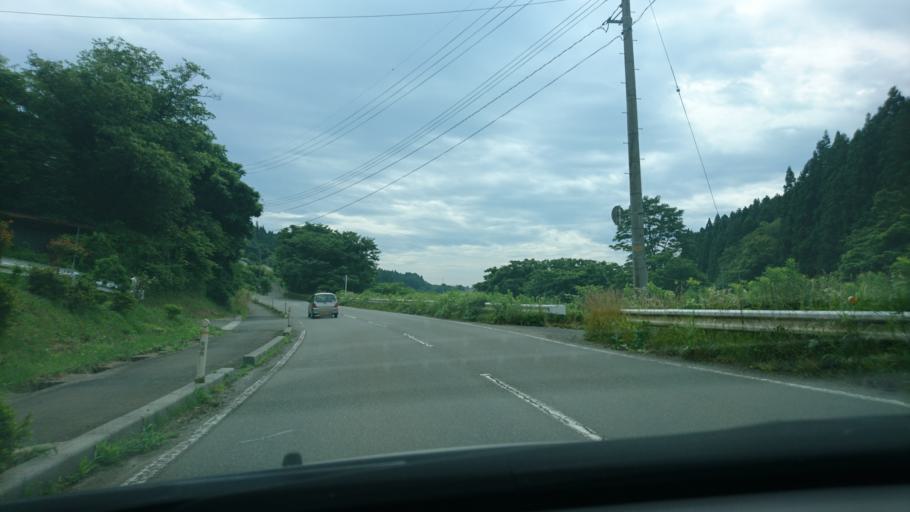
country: JP
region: Iwate
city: Ofunato
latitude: 38.7972
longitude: 141.4946
